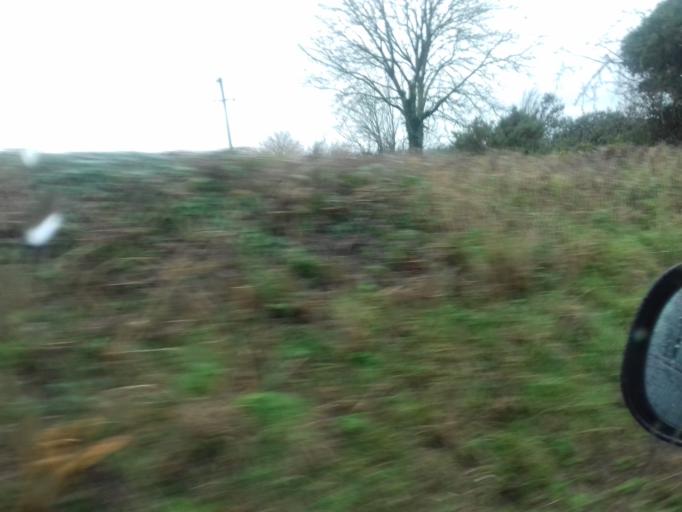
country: IE
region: Leinster
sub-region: Kilkenny
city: Graiguenamanagh
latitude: 52.5907
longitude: -7.0031
